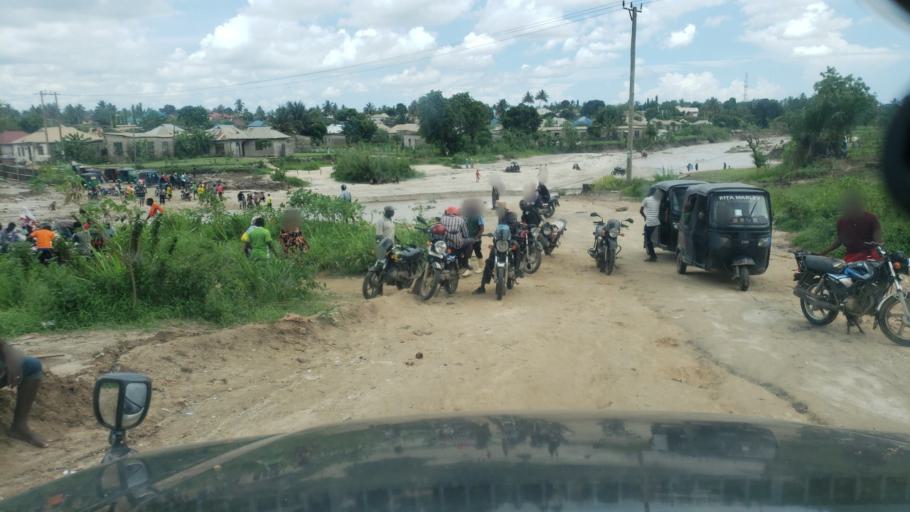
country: TZ
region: Pwani
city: Kisarawe
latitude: -6.8822
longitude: 39.1495
